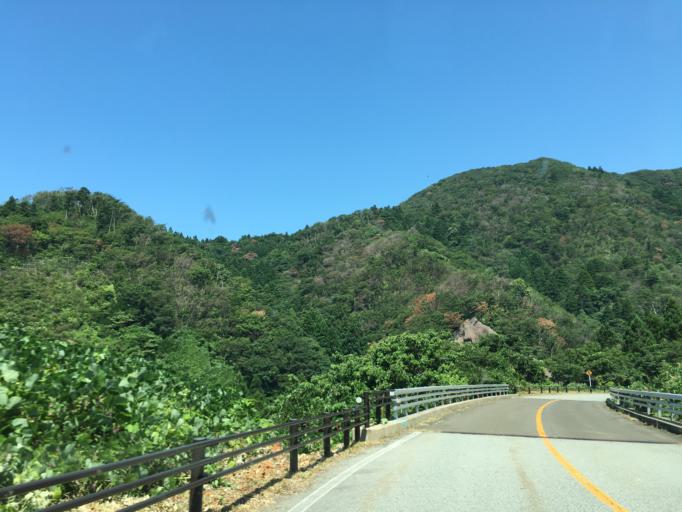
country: JP
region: Akita
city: Tenno
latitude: 39.9113
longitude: 139.7298
